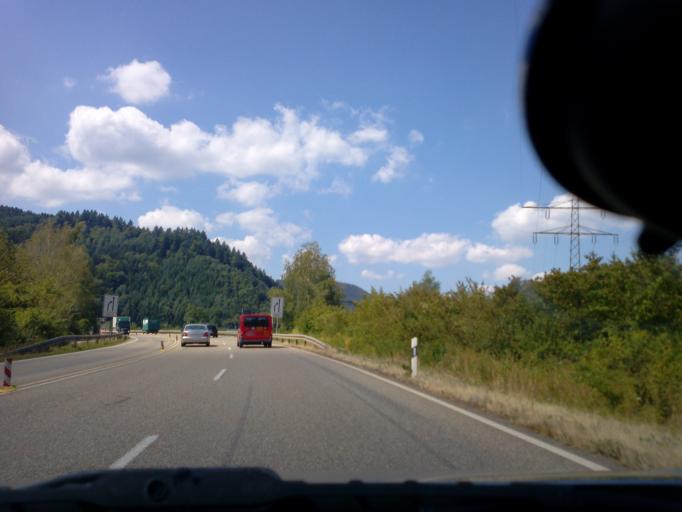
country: DE
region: Baden-Wuerttemberg
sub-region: Freiburg Region
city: Hausach
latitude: 48.2873
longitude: 8.1580
